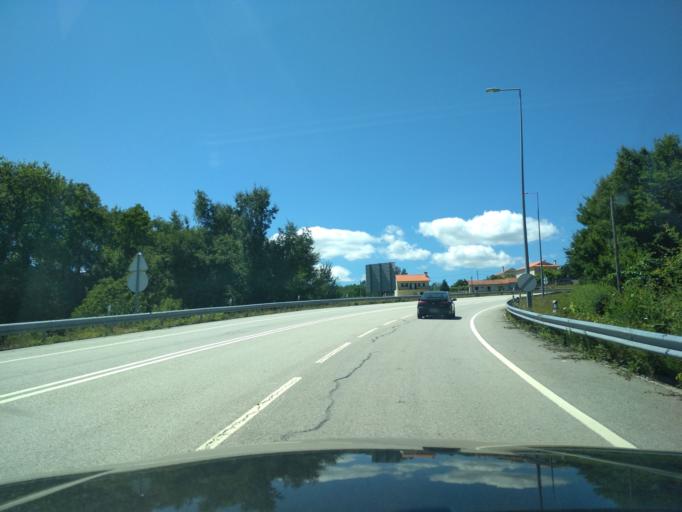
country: PT
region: Vila Real
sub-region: Ribeira de Pena
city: Ribeira de Pena
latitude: 41.5014
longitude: -7.7981
